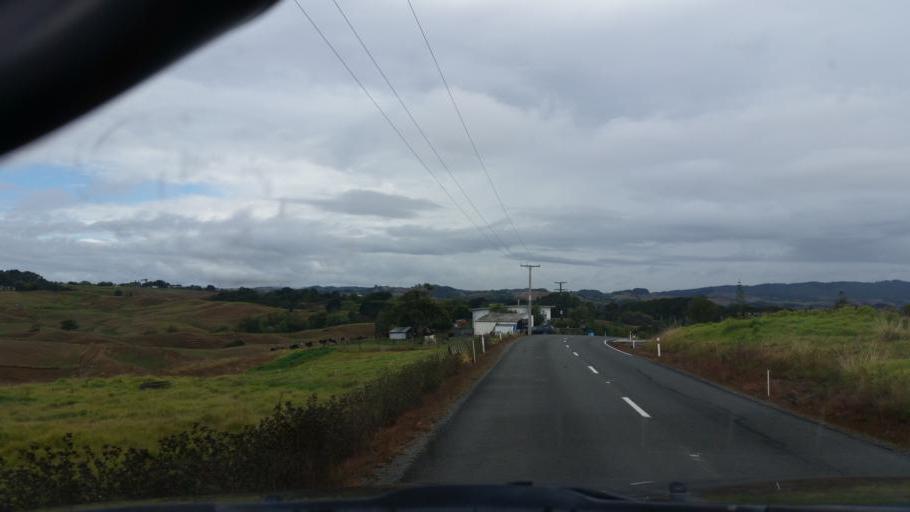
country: NZ
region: Auckland
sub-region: Auckland
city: Wellsford
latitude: -36.1271
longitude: 174.3579
